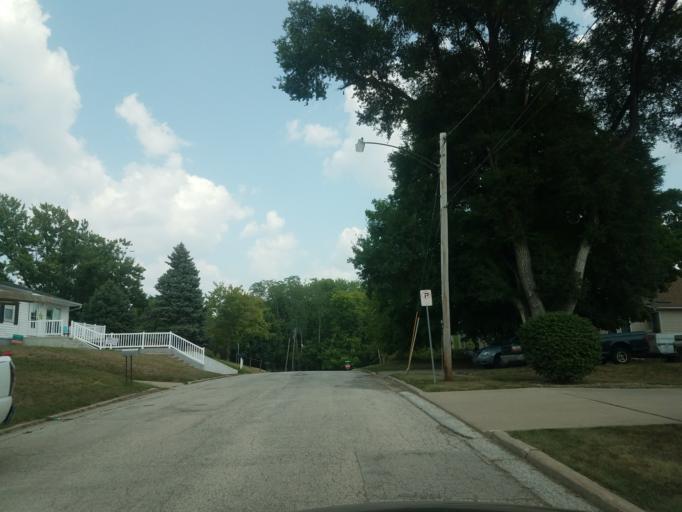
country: US
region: Illinois
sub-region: McLean County
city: Bloomington
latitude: 40.4651
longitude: -89.0019
